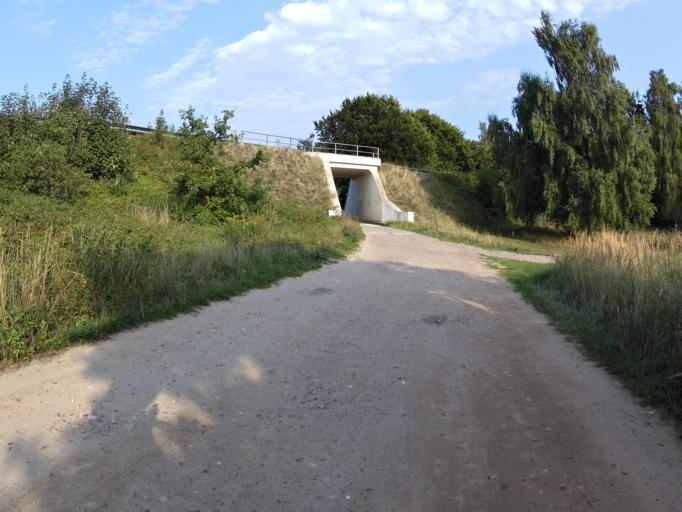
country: DE
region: Mecklenburg-Vorpommern
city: Seebad Bansin
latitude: 53.9606
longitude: 14.1396
